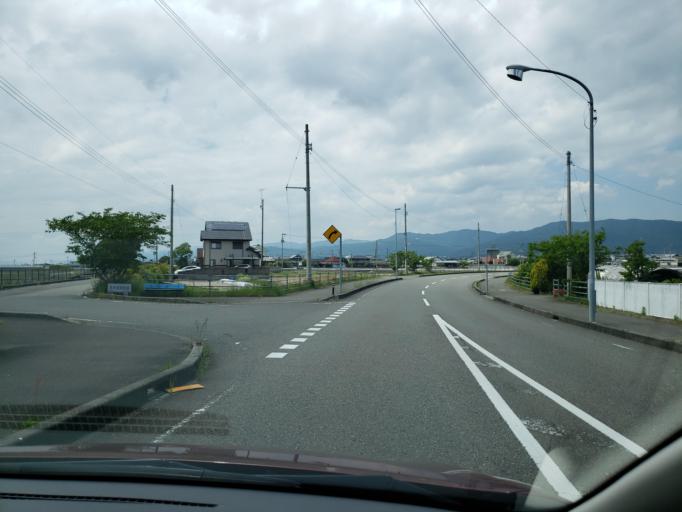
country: JP
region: Tokushima
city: Kamojimacho-jogejima
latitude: 34.0961
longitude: 134.3816
